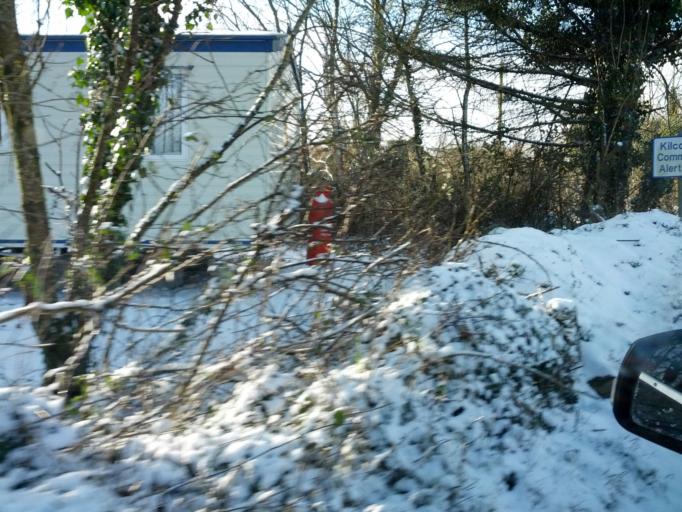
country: IE
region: Connaught
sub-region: County Galway
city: Athenry
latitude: 53.2121
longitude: -8.8168
